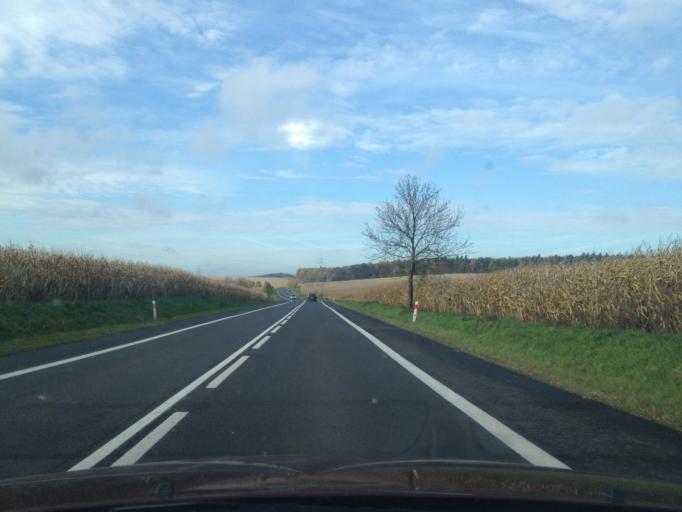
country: PL
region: Lower Silesian Voivodeship
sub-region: Powiat lubanski
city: Siekierczyn
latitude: 51.1451
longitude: 15.2036
